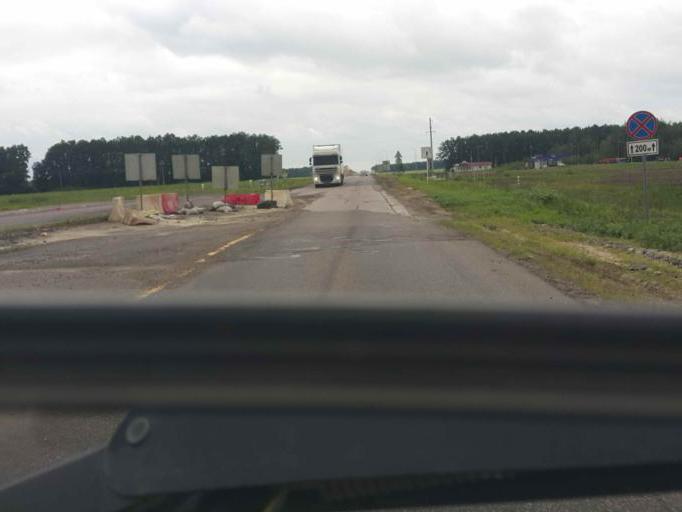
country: RU
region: Tambov
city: Zavoronezhskoye
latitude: 52.8905
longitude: 40.6996
